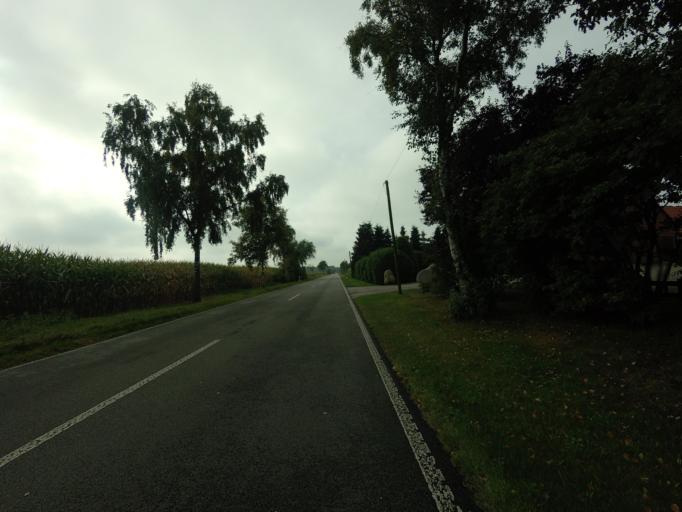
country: DE
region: Lower Saxony
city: Wielen
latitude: 52.5012
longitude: 6.7364
